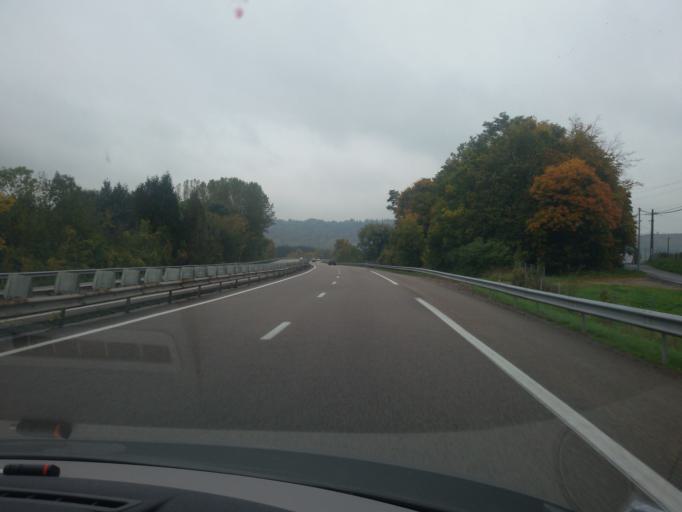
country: FR
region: Haute-Normandie
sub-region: Departement de l'Eure
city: Toutainville
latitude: 49.3593
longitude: 0.4649
